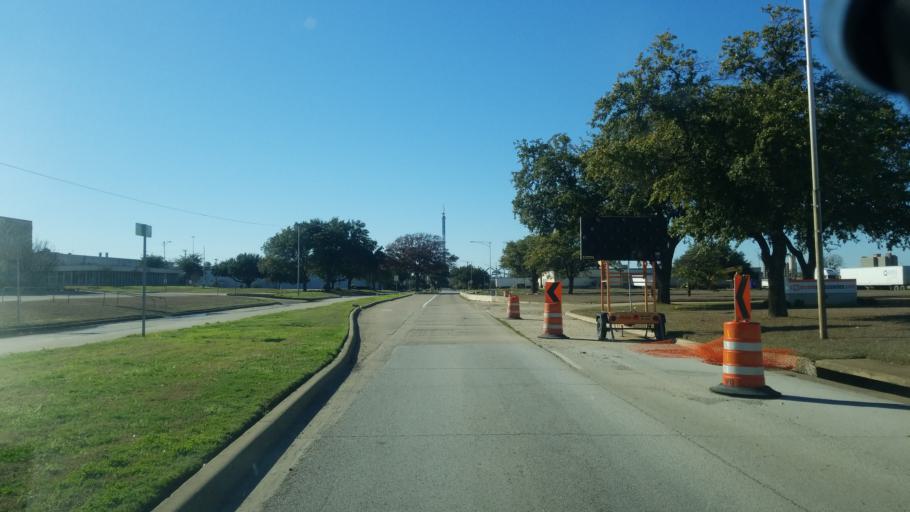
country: US
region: Texas
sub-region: Tarrant County
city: Arlington
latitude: 32.7566
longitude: -97.0559
